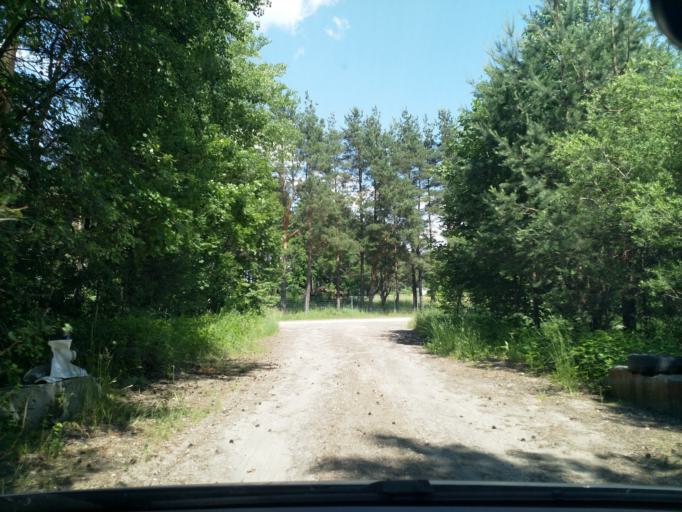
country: LV
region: Kuldigas Rajons
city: Kuldiga
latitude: 56.9701
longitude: 21.9268
